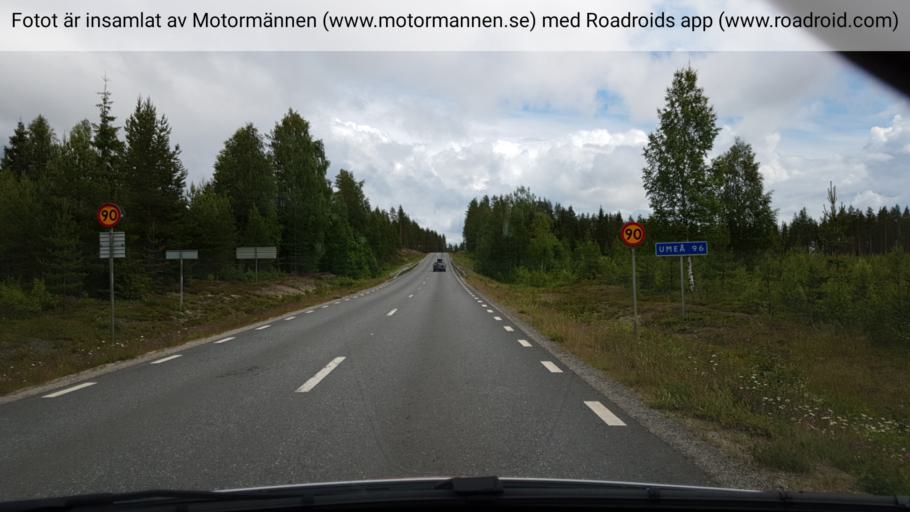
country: SE
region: Vaesterbotten
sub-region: Lycksele Kommun
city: Lycksele
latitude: 64.3962
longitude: 19.0595
